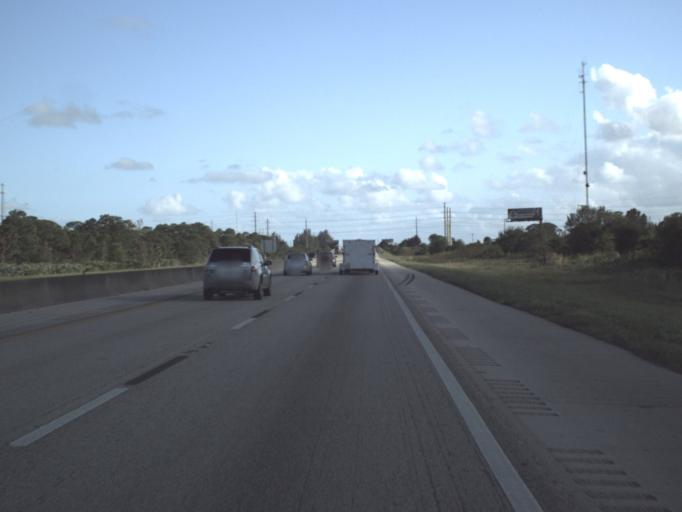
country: US
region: Florida
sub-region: Saint Lucie County
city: Fort Pierce South
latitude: 27.3870
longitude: -80.3902
